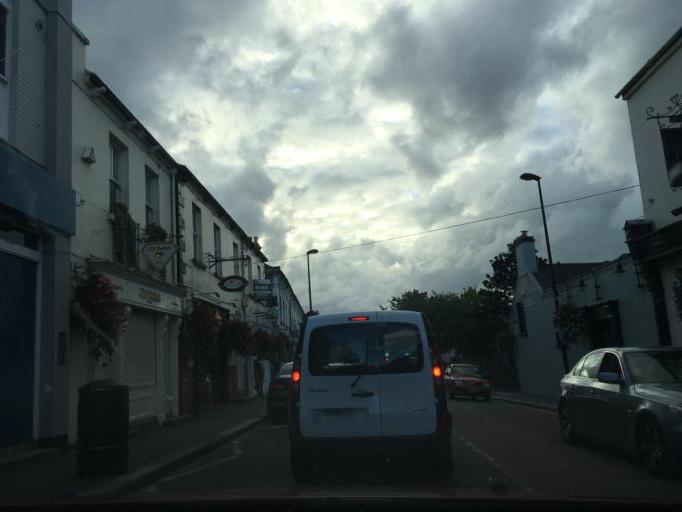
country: IE
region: Leinster
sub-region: Wicklow
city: Wicklow
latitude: 52.9805
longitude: -6.0424
